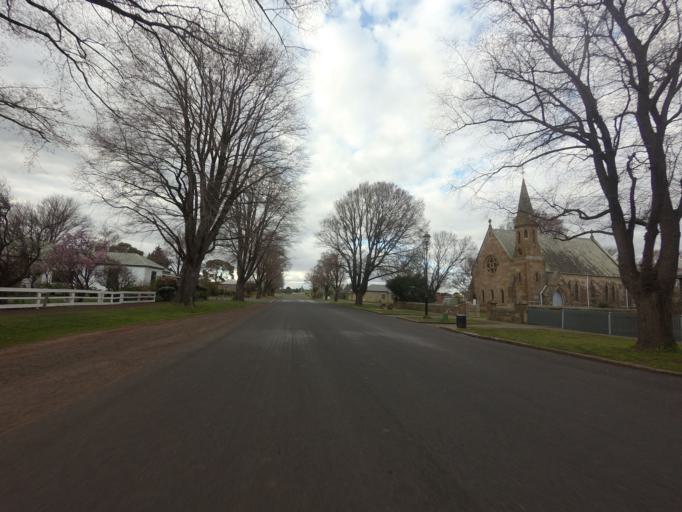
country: AU
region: Tasmania
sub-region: Northern Midlands
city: Evandale
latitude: -42.0273
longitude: 147.4930
